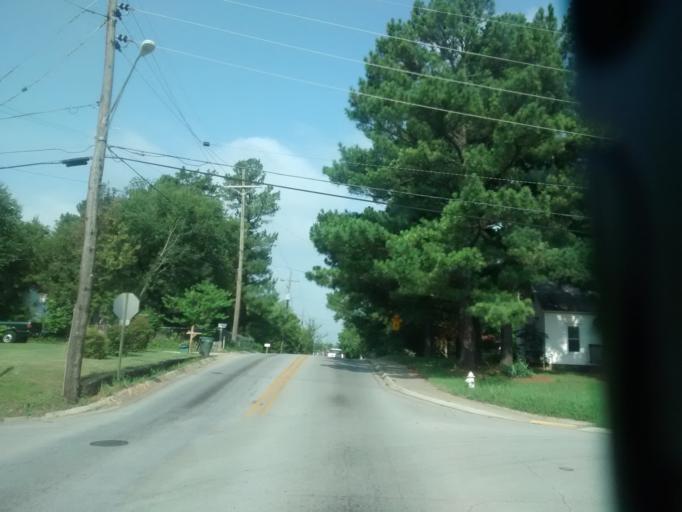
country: US
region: Arkansas
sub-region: Washington County
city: Fayetteville
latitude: 36.0560
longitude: -94.1516
